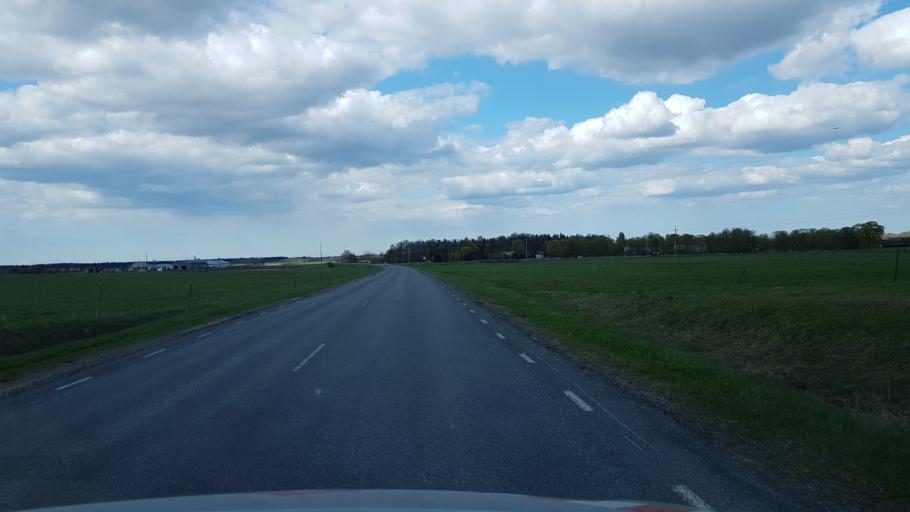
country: EE
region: Harju
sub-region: Keila linn
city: Keila
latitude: 59.2711
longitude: 24.4530
